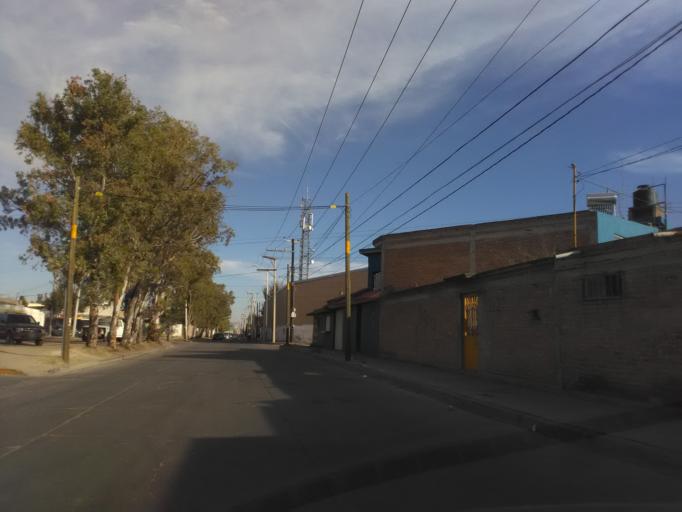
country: MX
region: Durango
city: Victoria de Durango
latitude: 24.0253
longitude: -104.6293
